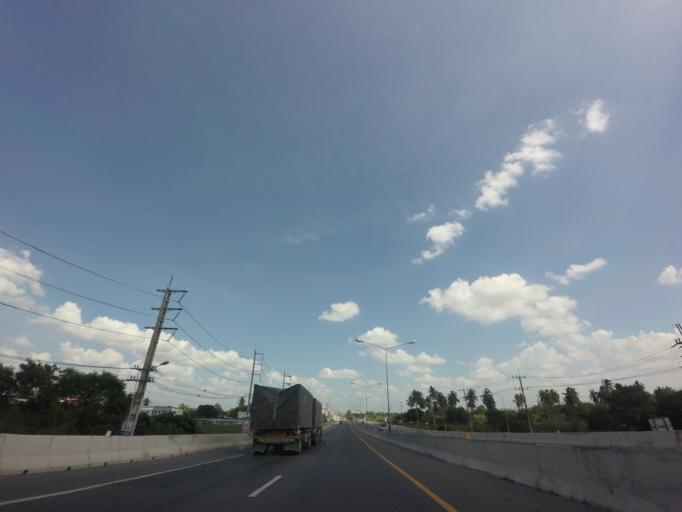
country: TH
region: Chon Buri
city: Ban Bueng
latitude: 13.3039
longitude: 101.1243
